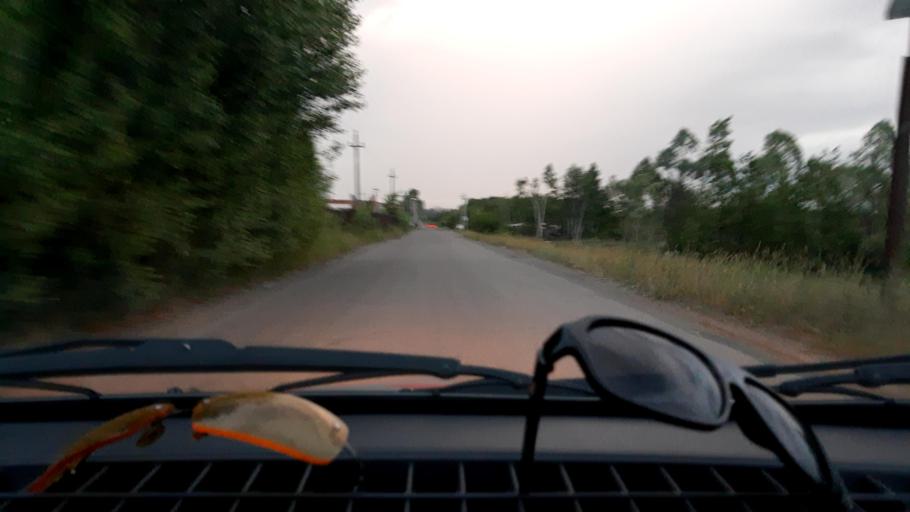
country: RU
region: Bashkortostan
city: Avdon
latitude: 54.6652
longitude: 55.8232
